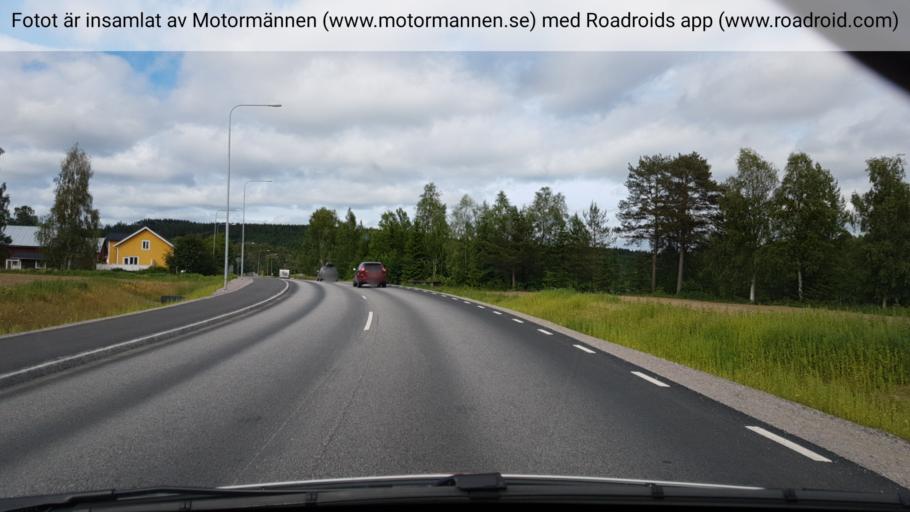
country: SE
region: Vaesterbotten
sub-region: Vannas Kommun
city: Vaennaes
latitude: 63.9140
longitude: 19.7734
